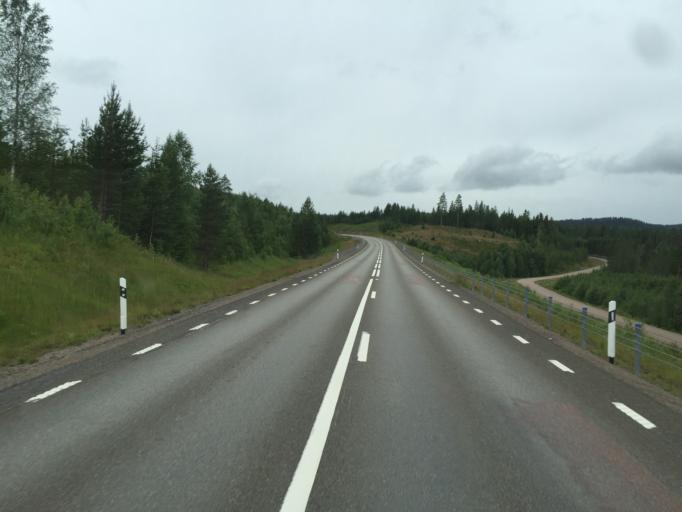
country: SE
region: Dalarna
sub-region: Malung-Saelens kommun
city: Malung
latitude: 60.6121
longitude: 13.5999
